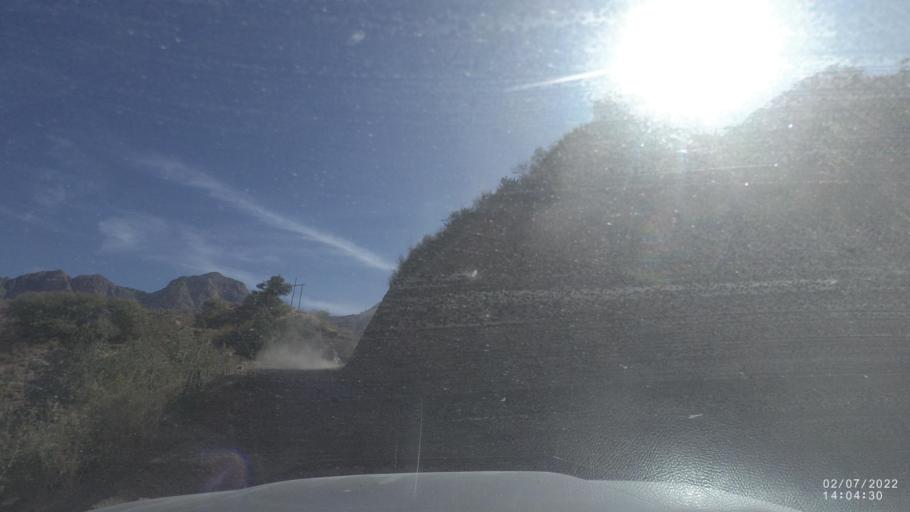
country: BO
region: Cochabamba
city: Irpa Irpa
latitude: -17.8224
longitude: -66.3939
